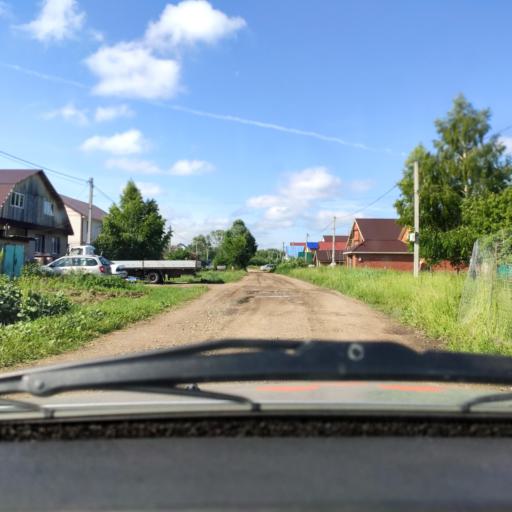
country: RU
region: Bashkortostan
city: Iglino
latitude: 54.7990
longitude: 56.2991
